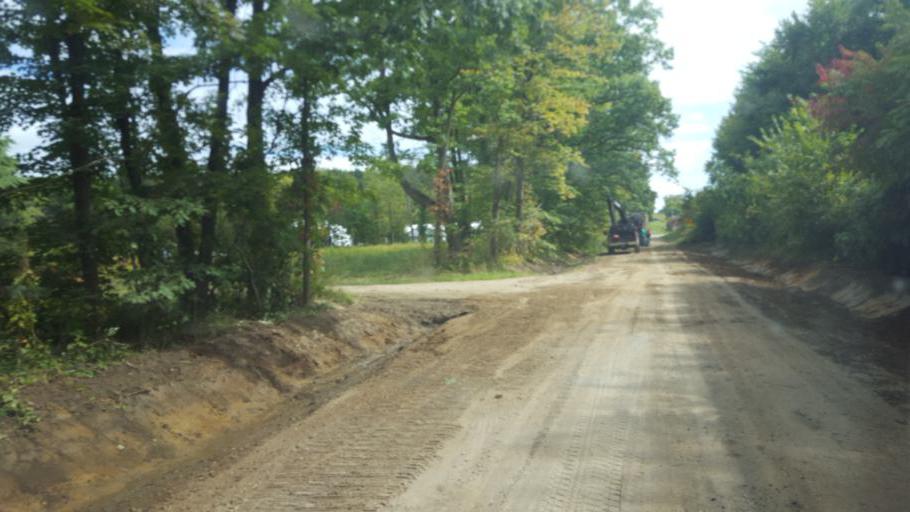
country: US
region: Pennsylvania
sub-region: Mercer County
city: Greenville
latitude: 41.4841
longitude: -80.3201
